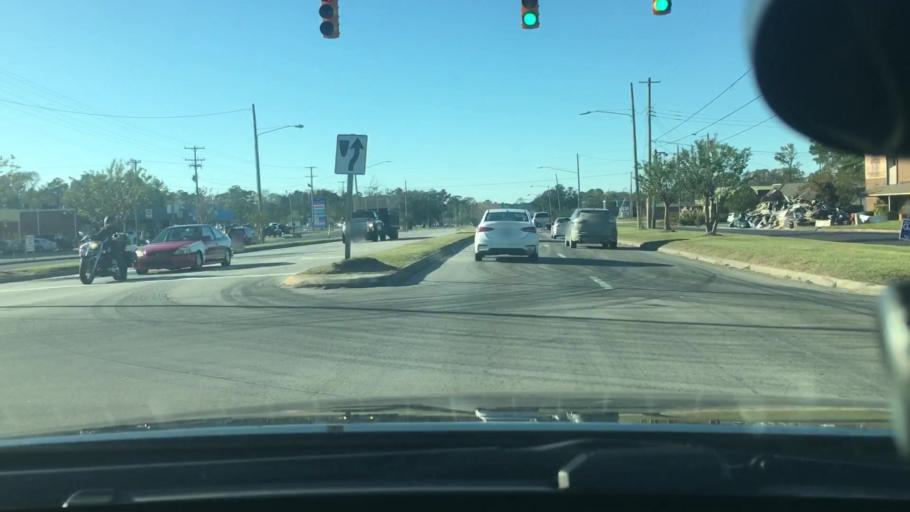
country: US
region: North Carolina
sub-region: Craven County
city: Havelock
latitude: 34.8867
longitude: -76.9162
